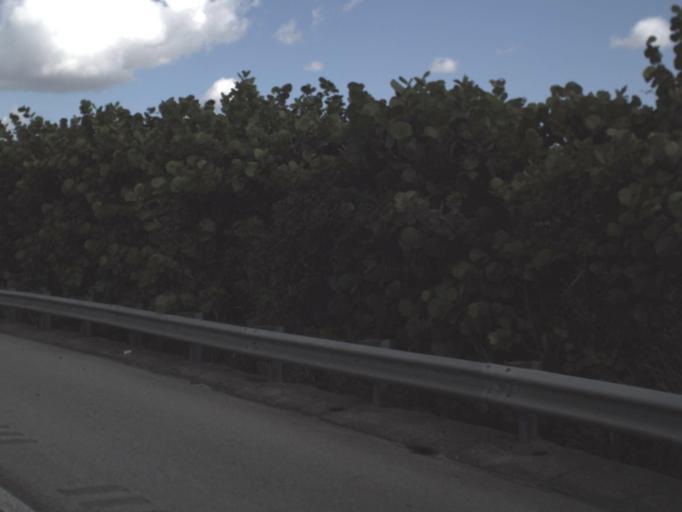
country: US
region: Florida
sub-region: Palm Beach County
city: Boca Pointe
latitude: 26.3363
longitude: -80.1702
